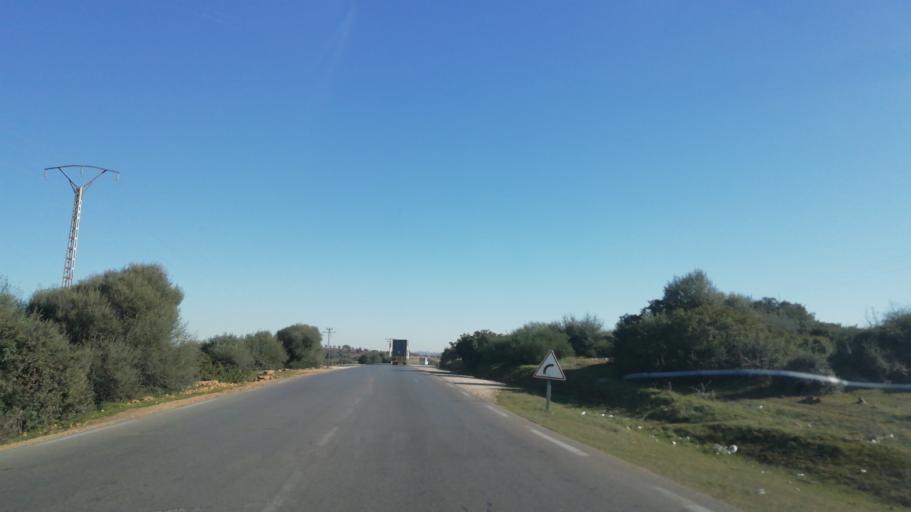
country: DZ
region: Relizane
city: Smala
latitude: 35.6906
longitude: 0.7922
